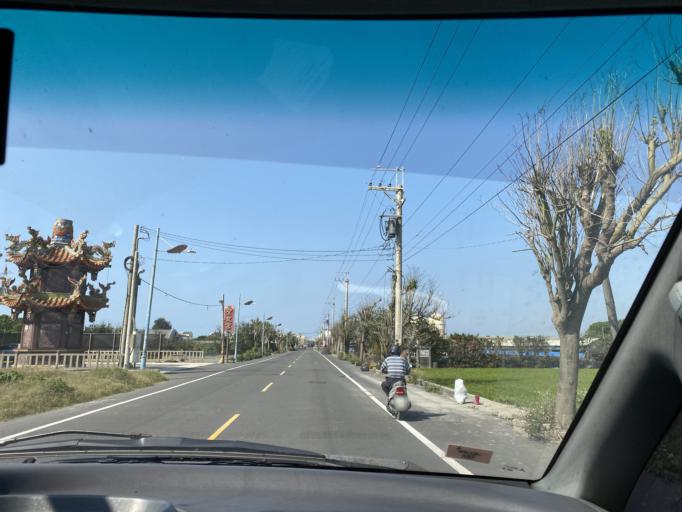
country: TW
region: Taiwan
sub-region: Changhua
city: Chang-hua
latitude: 23.9563
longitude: 120.3353
